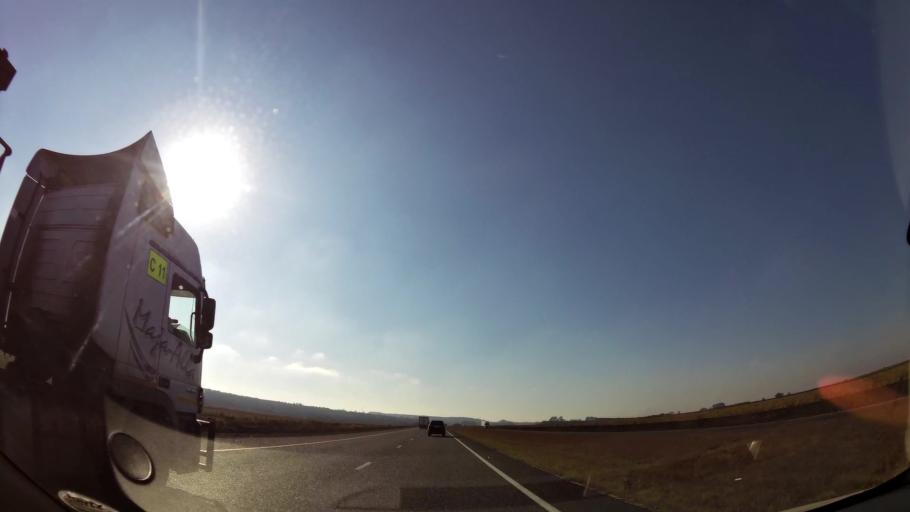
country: ZA
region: Mpumalanga
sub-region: Nkangala District Municipality
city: Delmas
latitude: -26.0182
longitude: 28.9359
